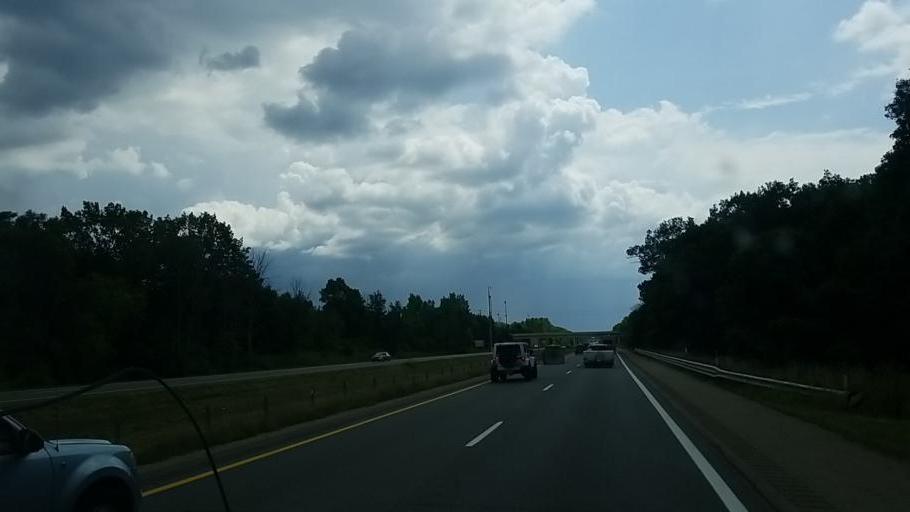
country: US
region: Michigan
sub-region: Kent County
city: Northview
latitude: 43.0021
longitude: -85.6050
